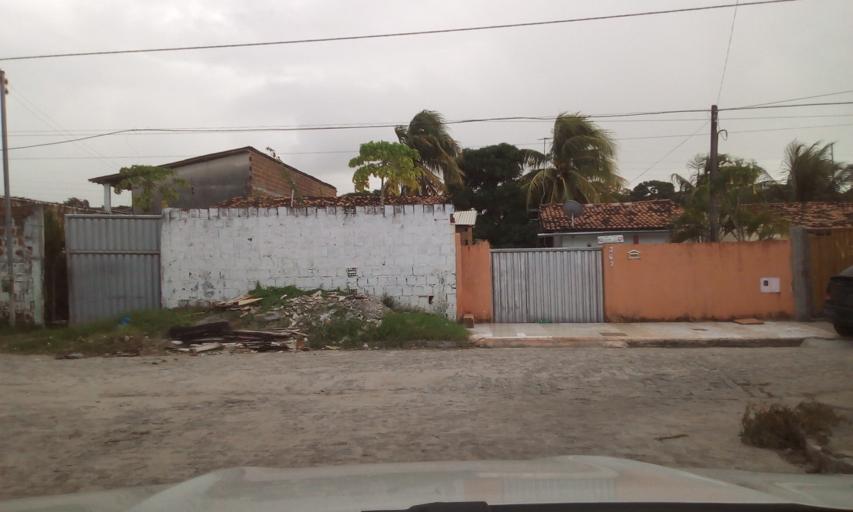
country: BR
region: Paraiba
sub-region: Joao Pessoa
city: Joao Pessoa
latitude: -7.0628
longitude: -34.8489
